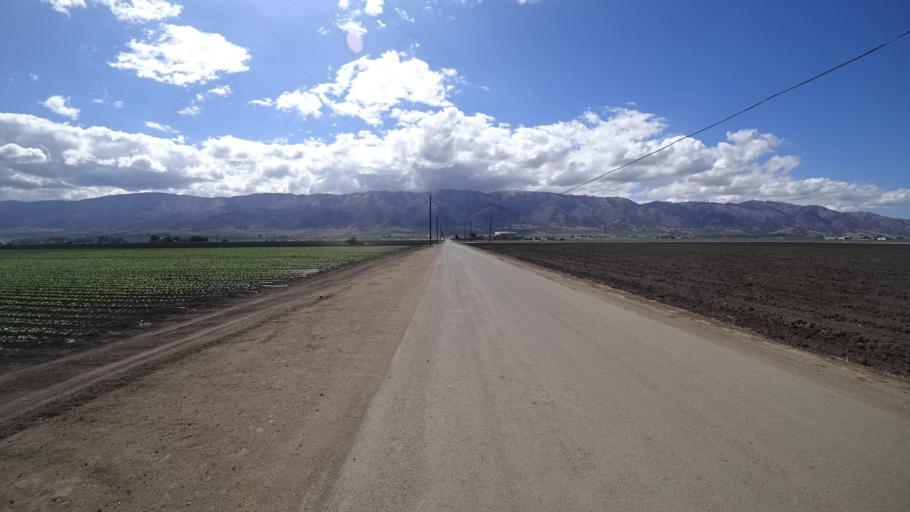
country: US
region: California
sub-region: Monterey County
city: Gonzales
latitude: 36.5111
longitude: -121.4722
